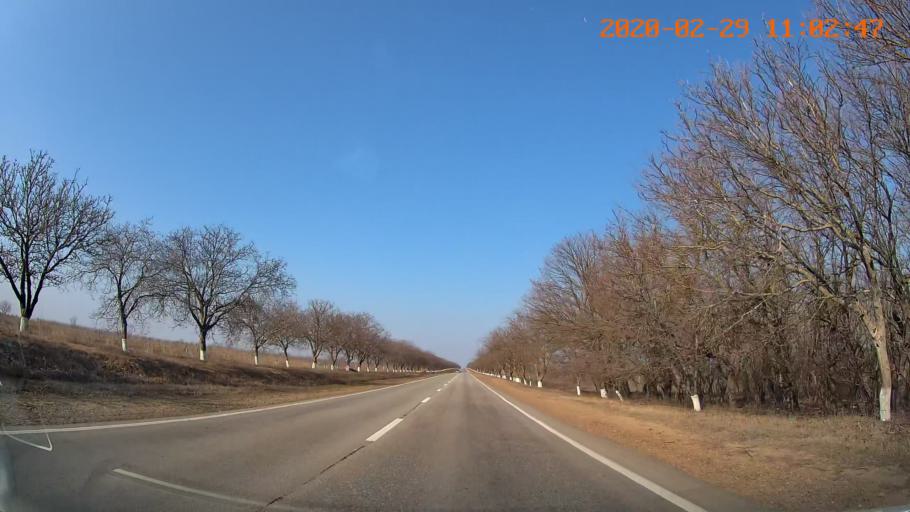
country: MD
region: Telenesti
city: Grigoriopol
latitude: 47.1749
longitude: 29.2312
